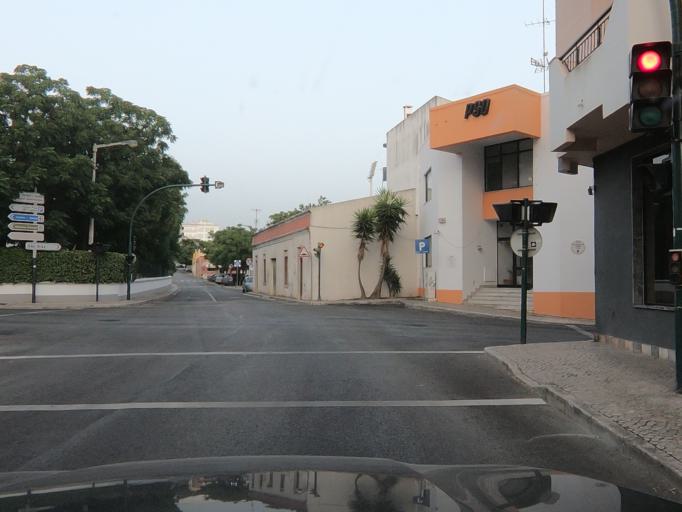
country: PT
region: Faro
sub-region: Loule
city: Loule
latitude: 37.1362
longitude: -8.0195
